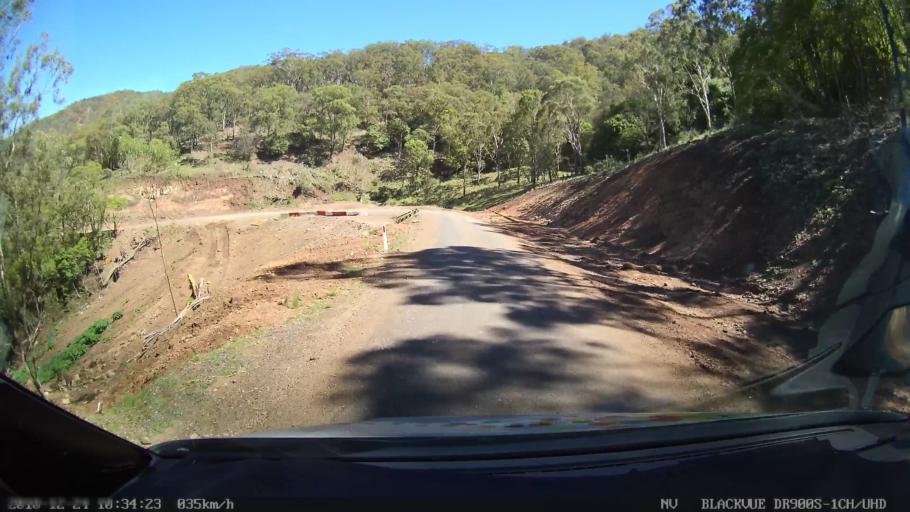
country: AU
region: New South Wales
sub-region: Upper Hunter Shire
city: Merriwa
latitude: -31.8424
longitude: 150.5055
